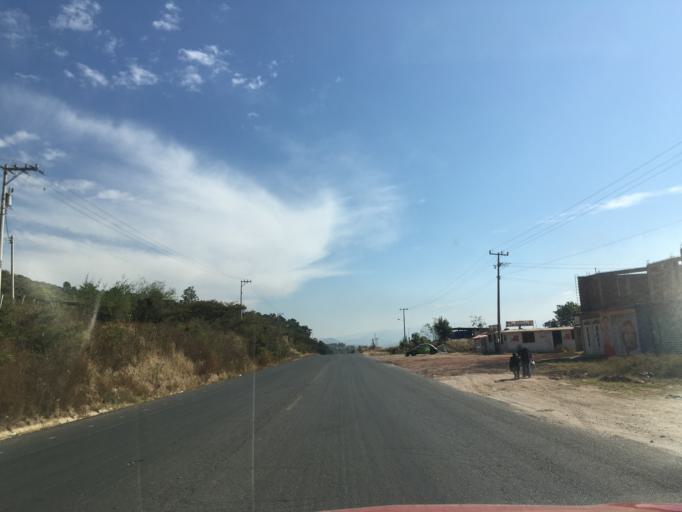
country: MX
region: Michoacan
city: Ciudad Hidalgo
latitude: 19.7067
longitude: -100.5646
